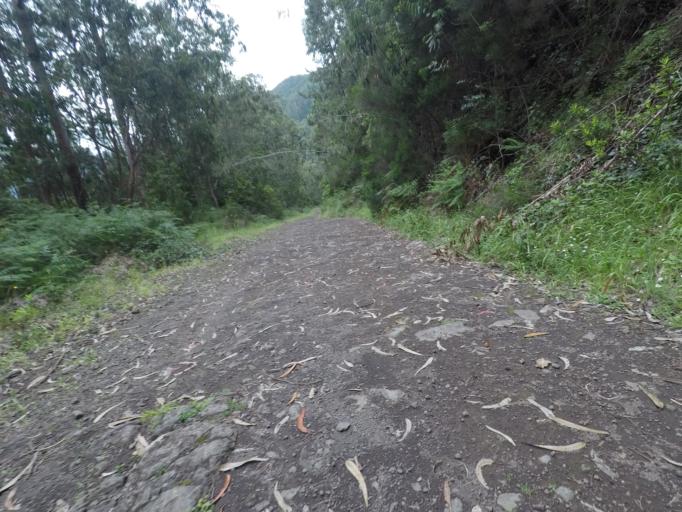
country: PT
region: Madeira
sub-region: Sao Vicente
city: Sao Vicente
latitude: 32.7757
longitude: -17.0494
